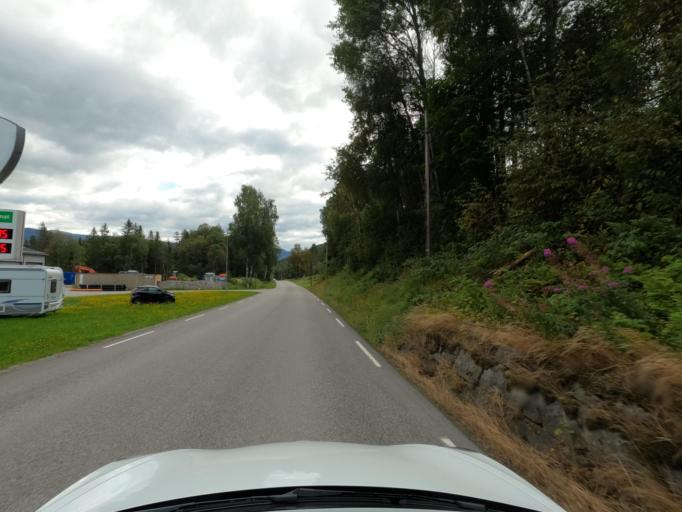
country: NO
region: Telemark
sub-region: Tinn
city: Rjukan
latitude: 59.9814
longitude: 8.7542
